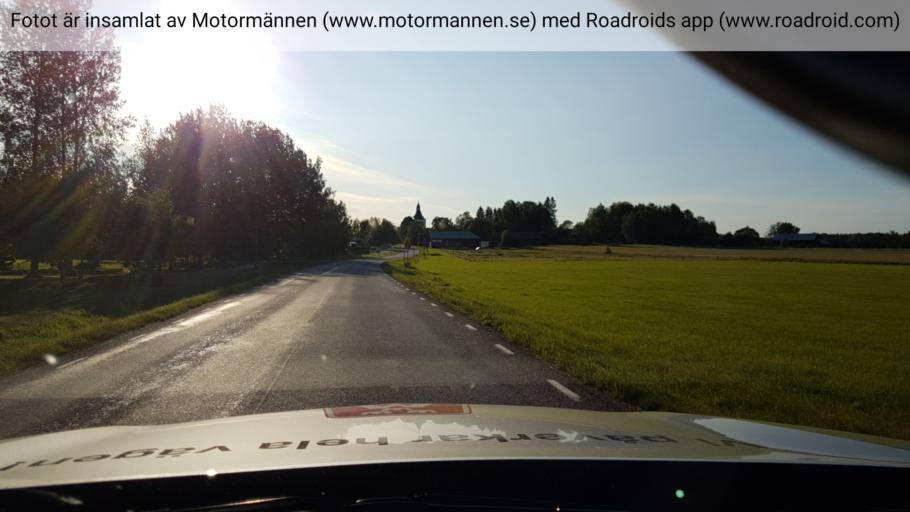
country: SE
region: Vaestmanland
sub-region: Surahammars Kommun
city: Ramnas
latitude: 59.9412
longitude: 16.2892
